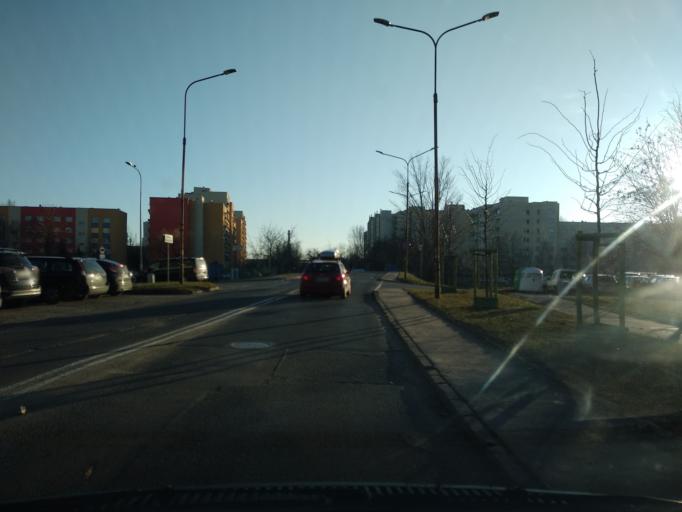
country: PL
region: Lower Silesian Voivodeship
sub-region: Powiat wroclawski
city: Wroclaw
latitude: 51.1254
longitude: 16.9682
